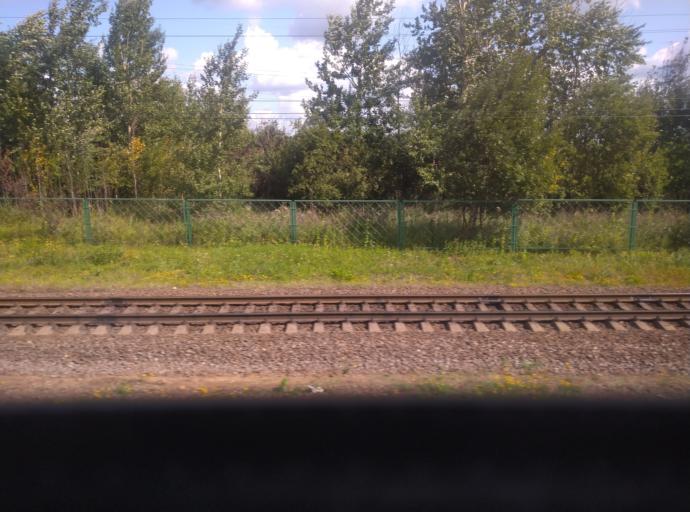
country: RU
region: St.-Petersburg
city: Kolpino
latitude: 59.7633
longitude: 30.5763
